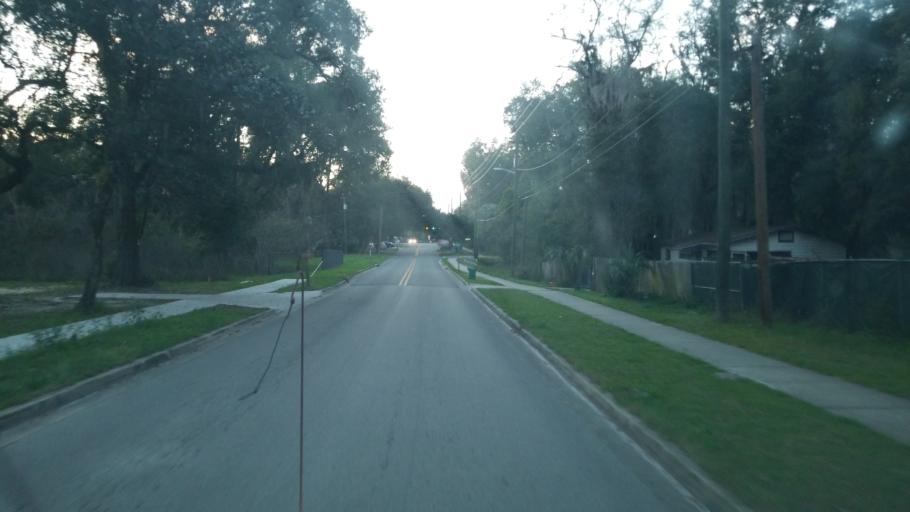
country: US
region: Florida
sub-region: Alachua County
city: Gainesville
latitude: 29.6501
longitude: -82.3087
